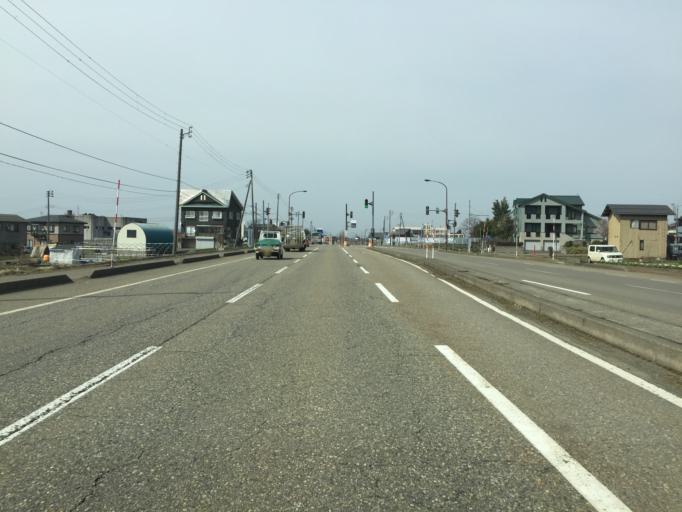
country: JP
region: Niigata
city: Ojiya
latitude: 37.3496
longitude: 138.8291
